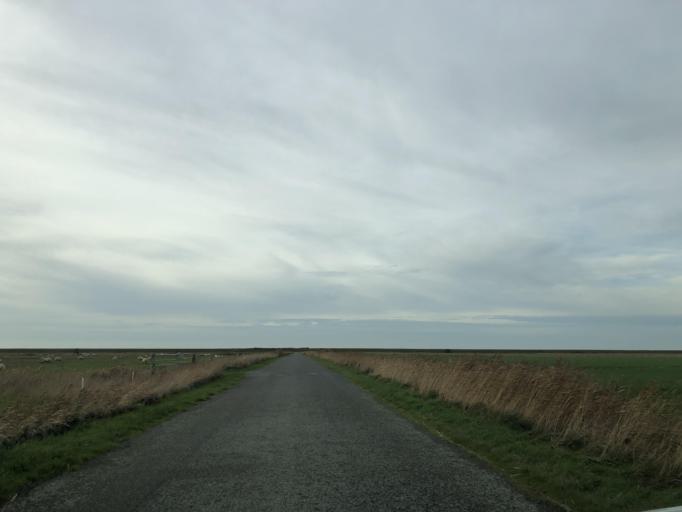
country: DK
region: South Denmark
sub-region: Tonder Kommune
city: Sherrebek
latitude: 55.1918
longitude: 8.6948
